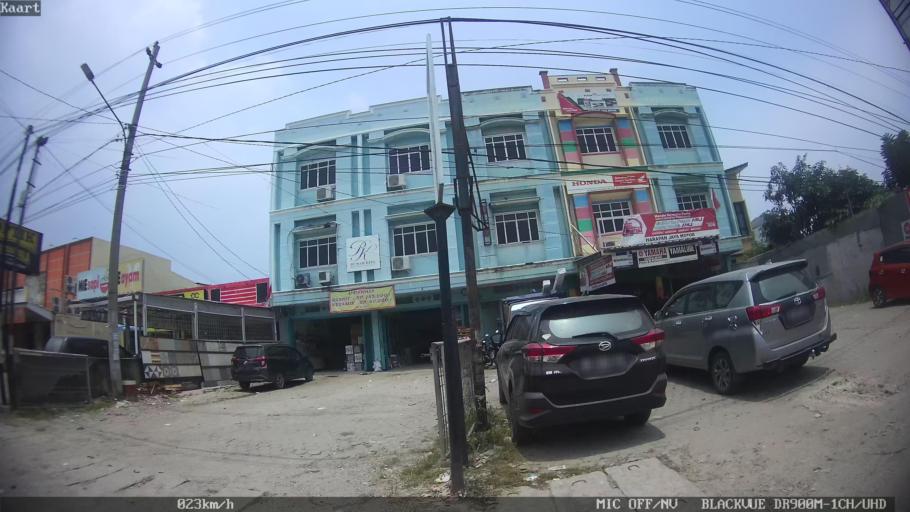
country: ID
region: Lampung
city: Kedaton
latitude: -5.3955
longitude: 105.2974
